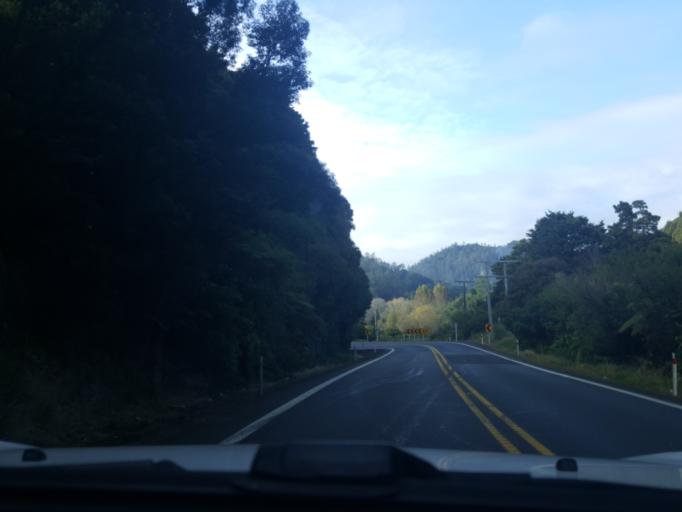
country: NZ
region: Waikato
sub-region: Hauraki District
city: Paeroa
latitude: -37.4125
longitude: 175.7104
